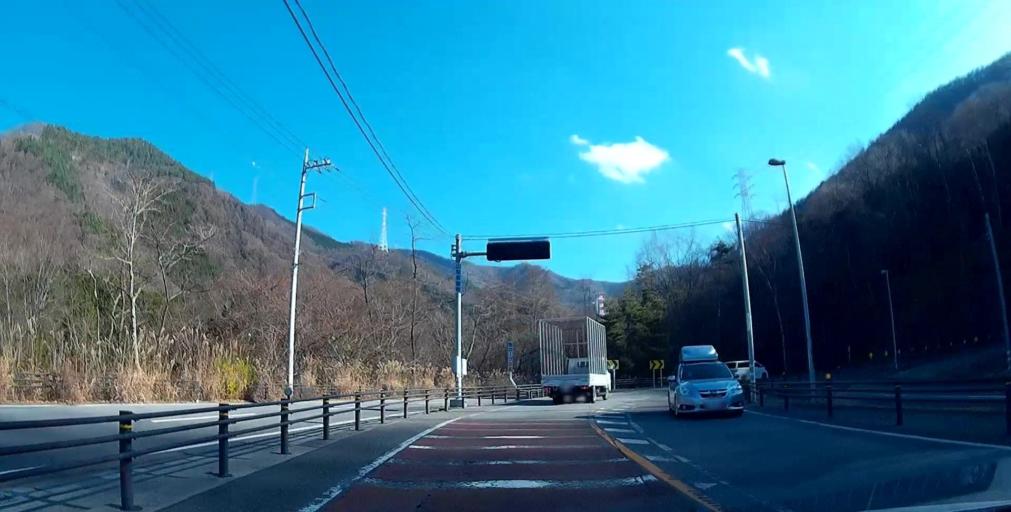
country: JP
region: Yamanashi
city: Fujikawaguchiko
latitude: 35.5736
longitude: 138.7696
